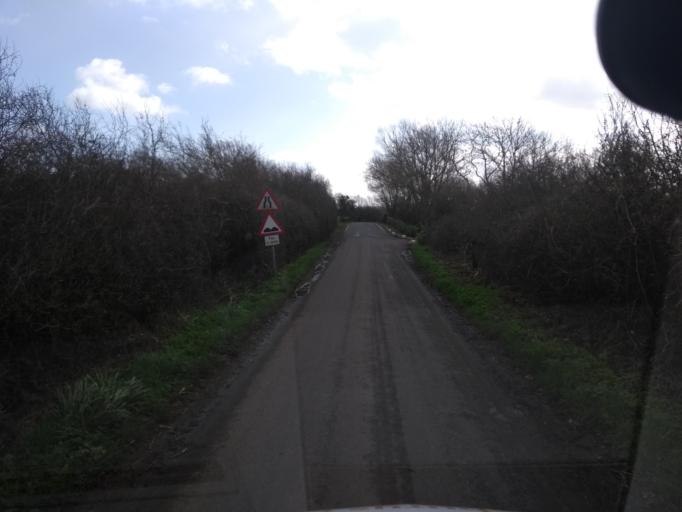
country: GB
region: England
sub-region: Somerset
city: Curry Rivel
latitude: 50.9906
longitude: -2.8546
